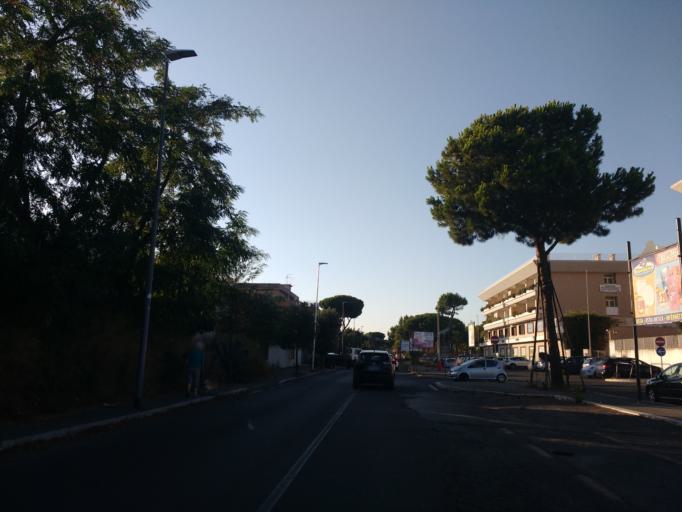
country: IT
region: Latium
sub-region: Citta metropolitana di Roma Capitale
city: Vitinia
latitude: 41.7750
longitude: 12.3703
